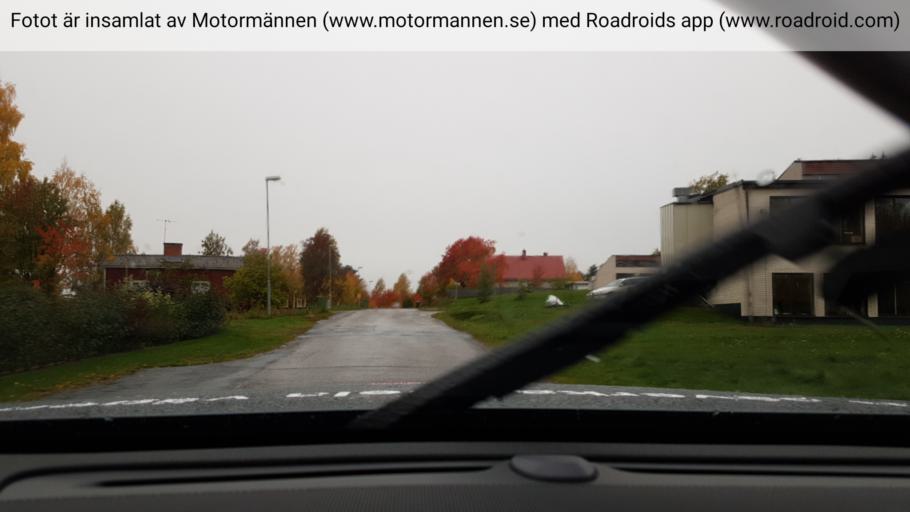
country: SE
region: Norrbotten
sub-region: Lulea Kommun
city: Sodra Sunderbyn
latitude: 65.6591
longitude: 21.9477
